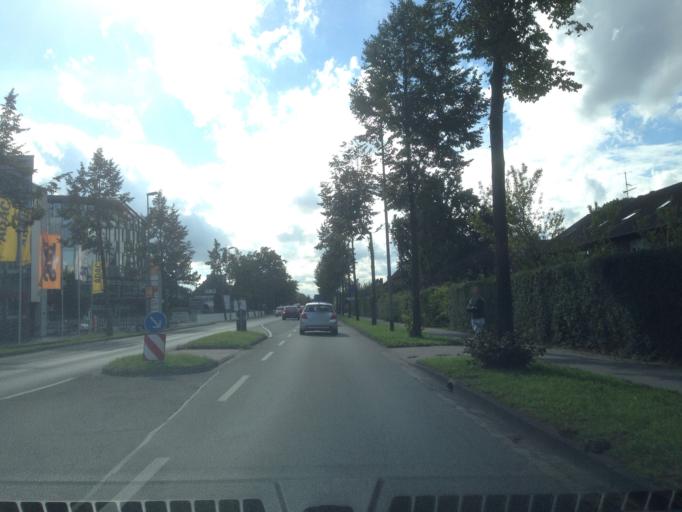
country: DE
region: North Rhine-Westphalia
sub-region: Regierungsbezirk Munster
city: Muenster
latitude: 51.9281
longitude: 7.5877
